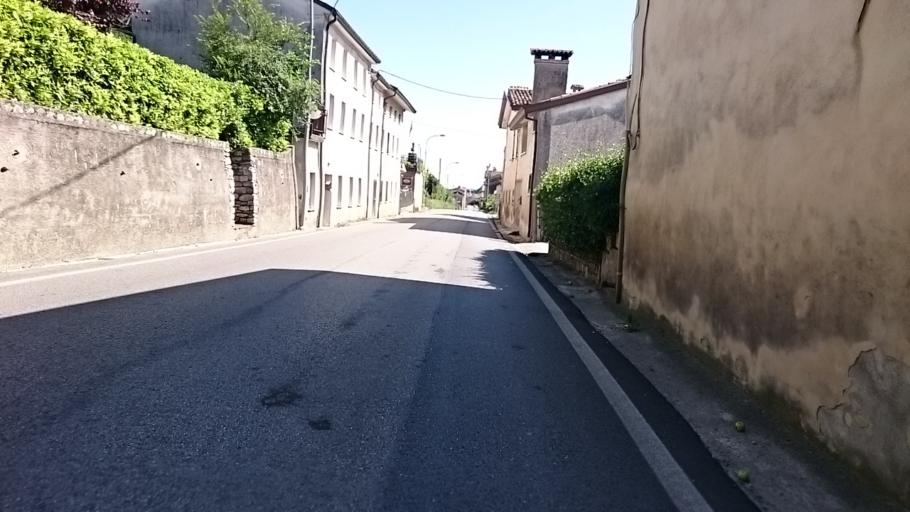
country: IT
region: Veneto
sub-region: Provincia di Treviso
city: Col San Martino
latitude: 45.9048
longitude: 12.0786
